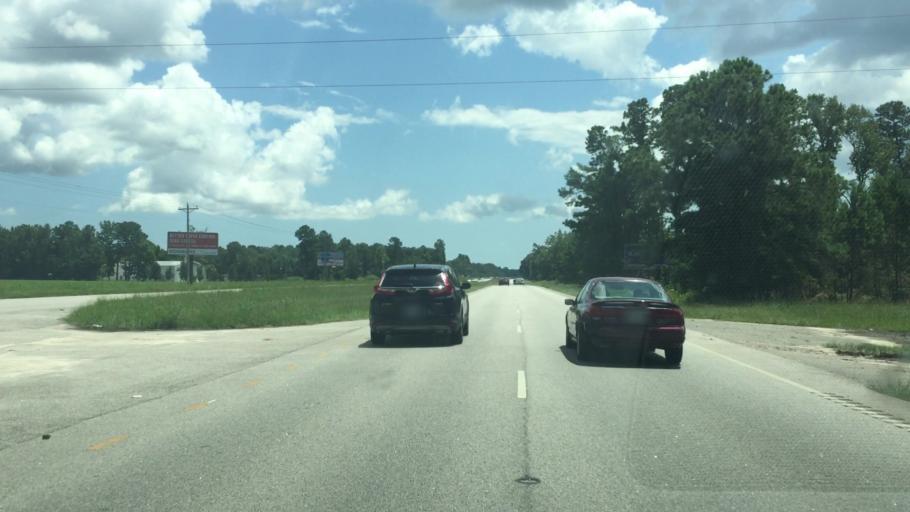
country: US
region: South Carolina
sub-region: Horry County
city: Little River
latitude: 33.9722
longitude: -78.7416
